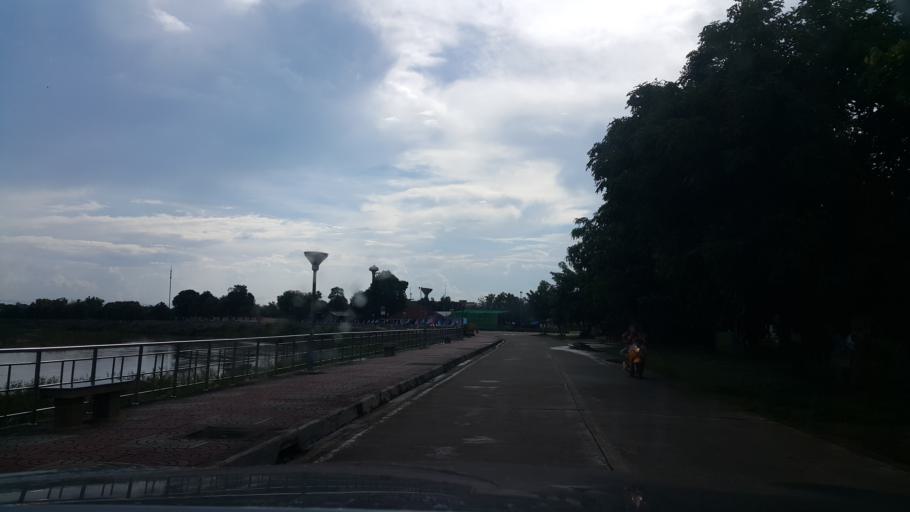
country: TH
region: Lampang
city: Thoen
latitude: 17.6154
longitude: 99.2217
